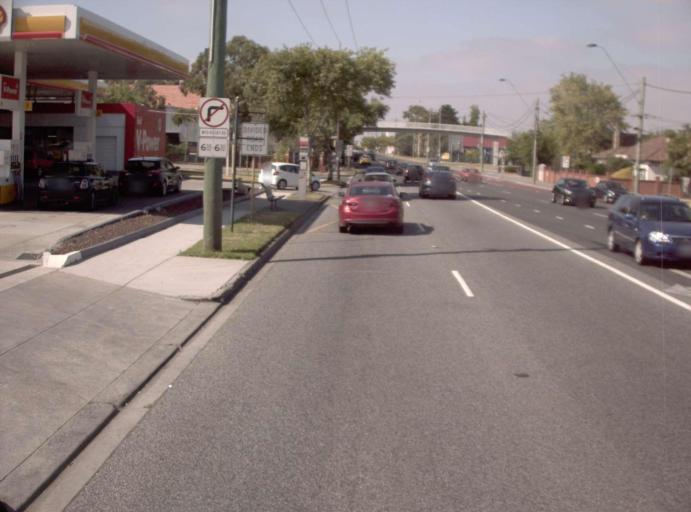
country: AU
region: Victoria
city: Hughesdale
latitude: -37.8936
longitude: 145.0882
